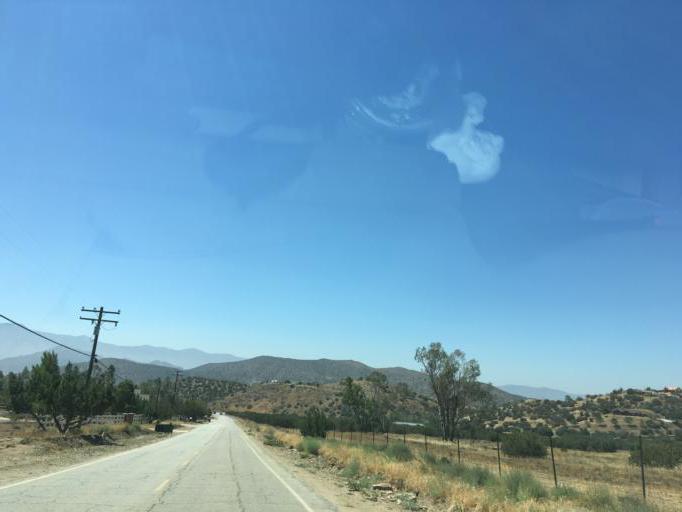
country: US
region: California
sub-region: Los Angeles County
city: Acton
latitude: 34.5208
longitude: -118.2380
